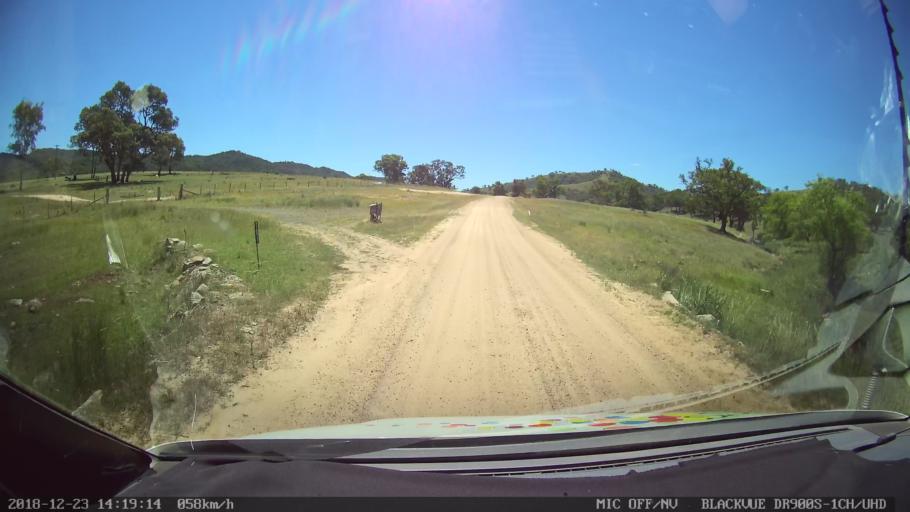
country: AU
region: New South Wales
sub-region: Tamworth Municipality
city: Manilla
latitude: -30.6540
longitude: 150.9981
